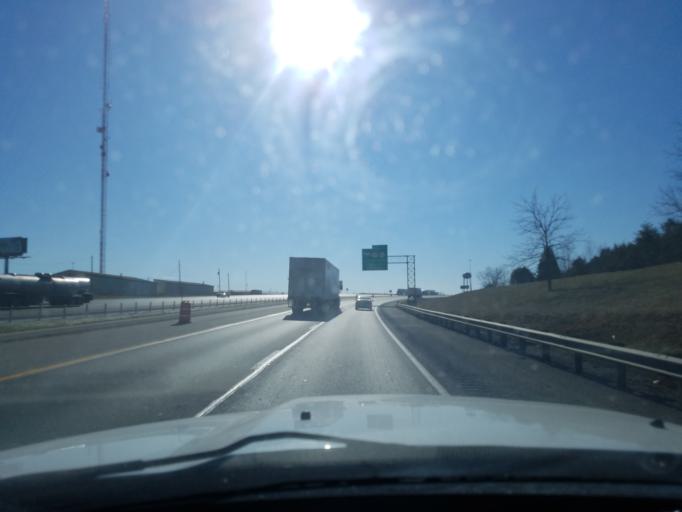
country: US
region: Kentucky
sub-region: Hardin County
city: Elizabethtown
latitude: 37.6826
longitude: -85.8435
